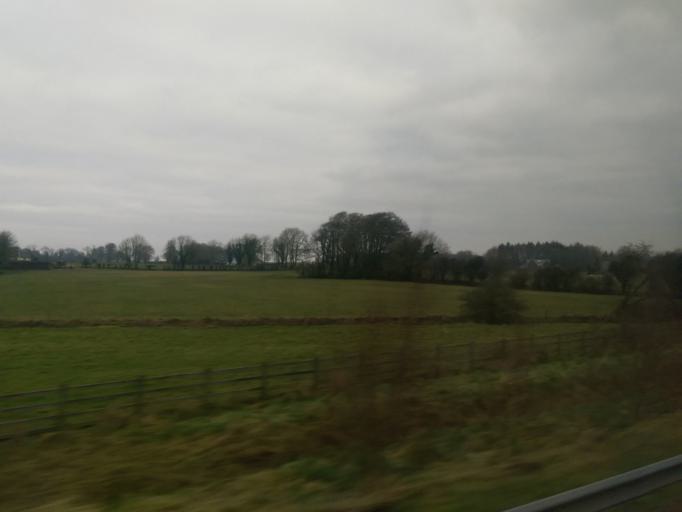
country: IE
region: Connaught
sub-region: County Galway
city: Ballinasloe
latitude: 53.3034
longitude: -8.3359
